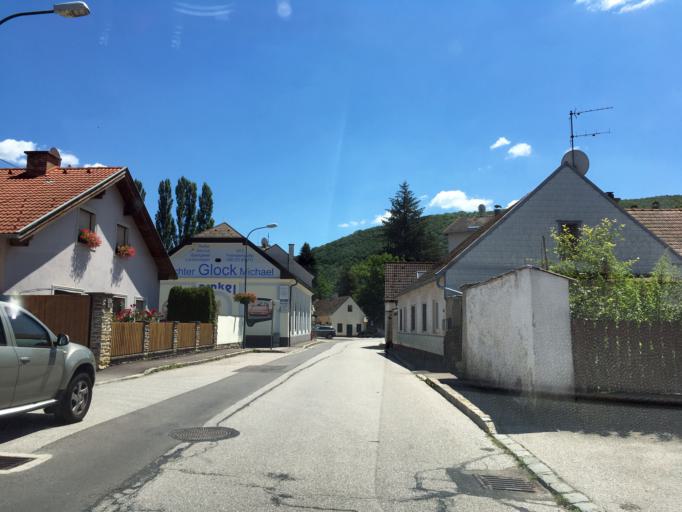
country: AT
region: Lower Austria
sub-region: Politischer Bezirk Neunkirchen
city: Seebenstein
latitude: 47.7015
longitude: 16.1433
